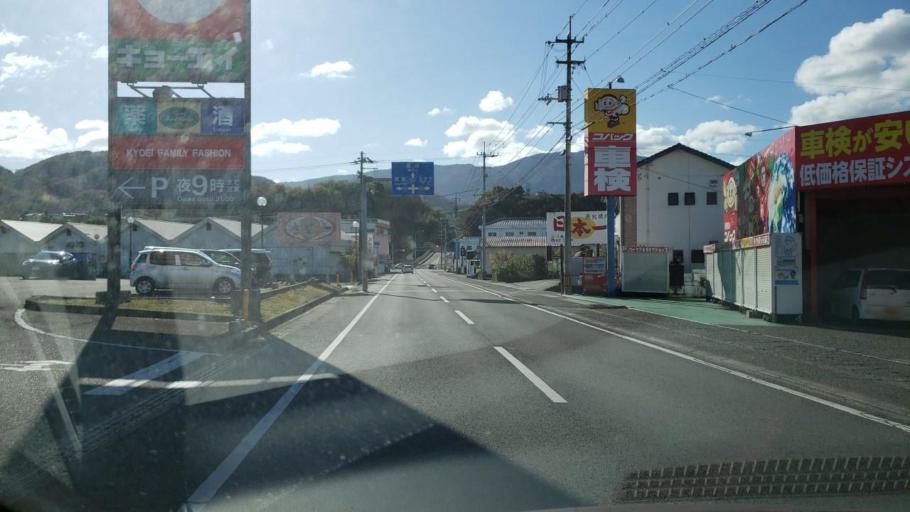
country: JP
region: Tokushima
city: Wakimachi
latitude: 34.0588
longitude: 134.2384
